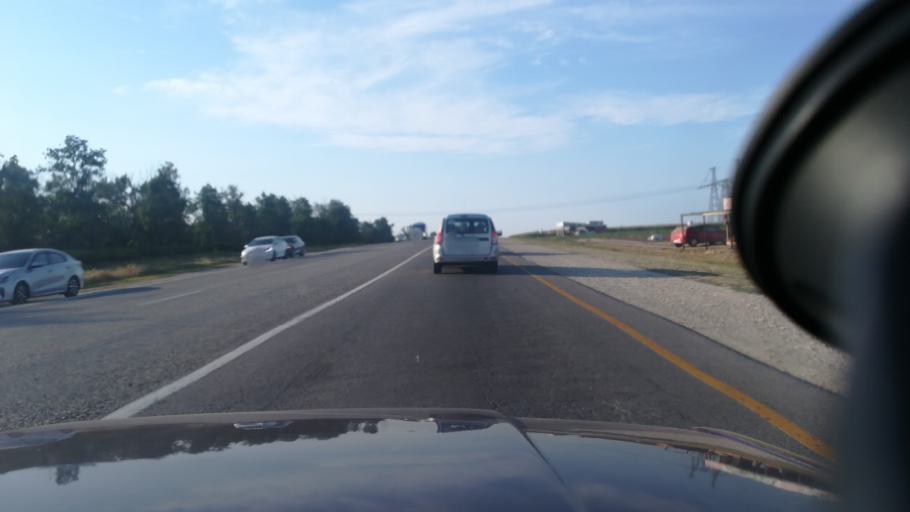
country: RU
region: Krasnodarskiy
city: Dzhiginka
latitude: 45.1080
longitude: 37.3172
